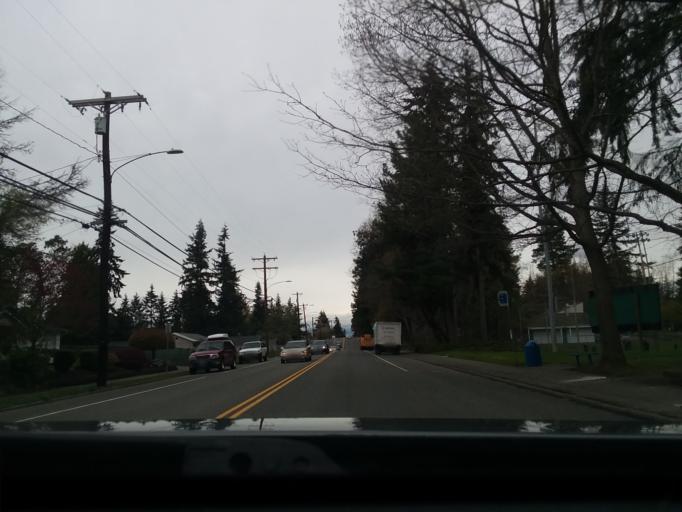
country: US
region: Washington
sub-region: Snohomish County
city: Mountlake Terrace
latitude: 47.7958
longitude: -122.3085
